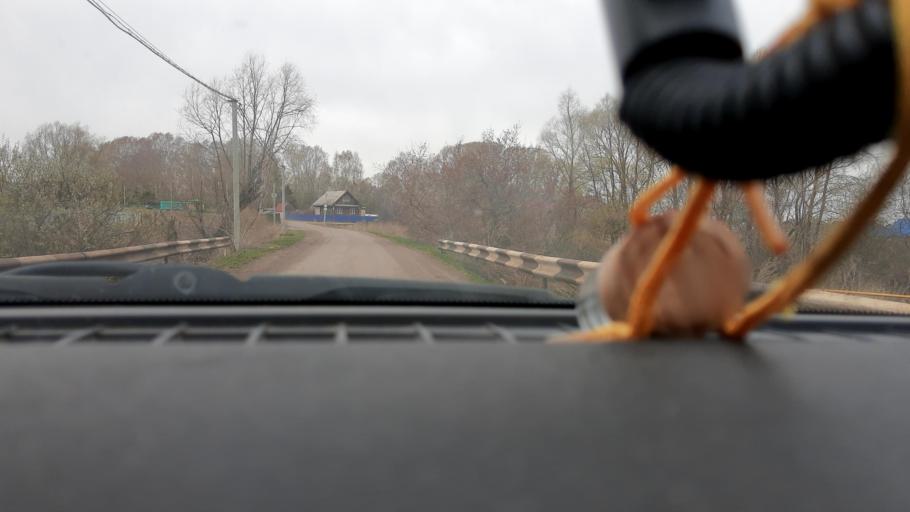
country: RU
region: Bashkortostan
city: Asanovo
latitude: 54.8143
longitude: 55.5644
